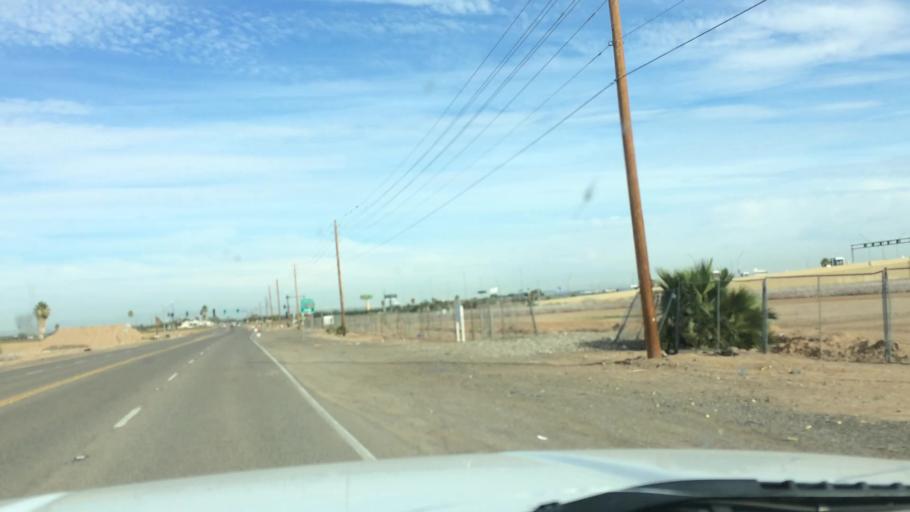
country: US
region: Arizona
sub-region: Maricopa County
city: Peoria
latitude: 33.5278
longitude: -112.2725
